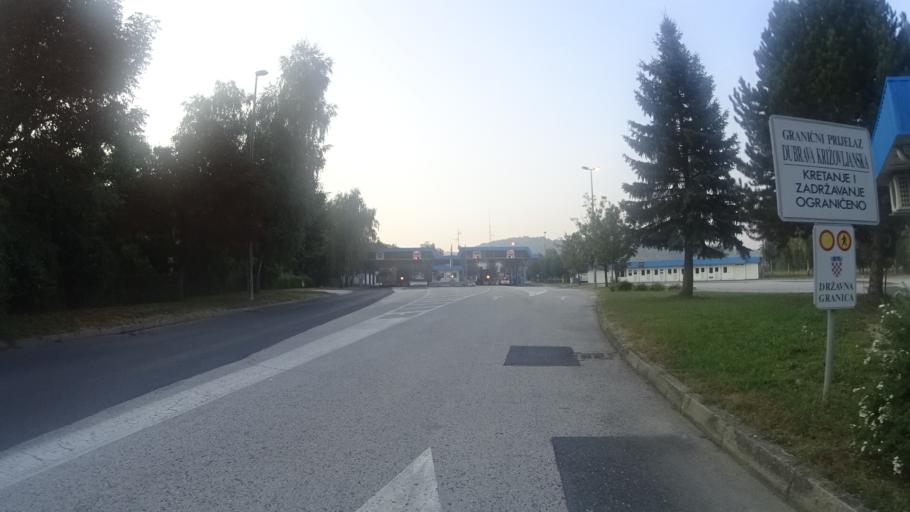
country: SI
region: Zavrc
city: Zavrc
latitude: 46.3865
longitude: 16.0557
